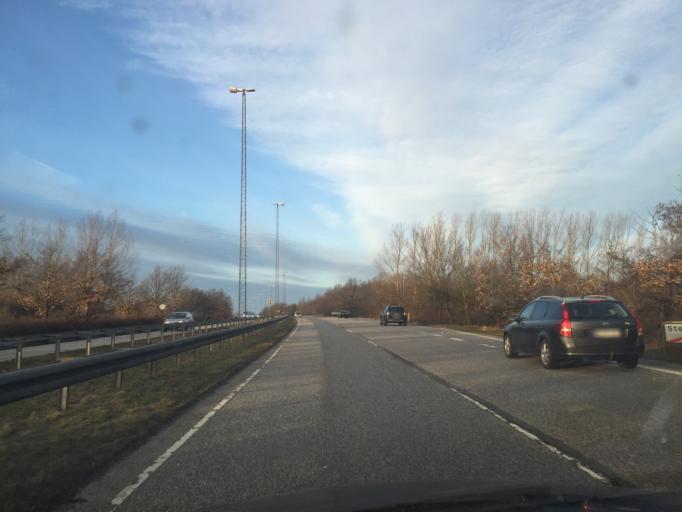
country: DK
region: Capital Region
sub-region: Hoje-Taastrup Kommune
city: Taastrup
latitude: 55.6624
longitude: 12.2820
